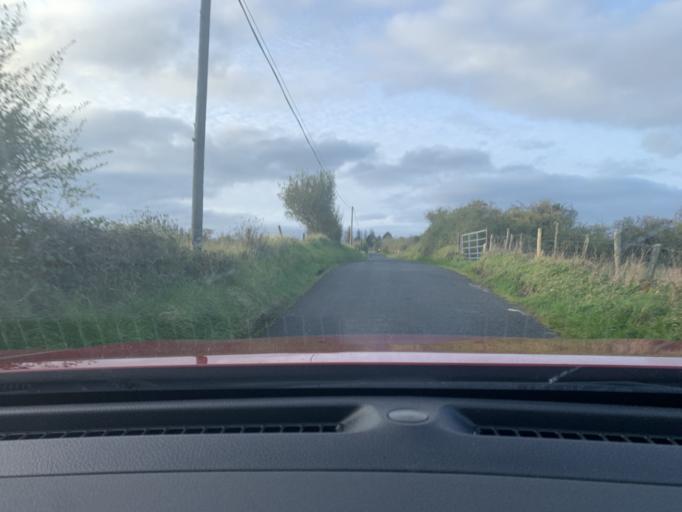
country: IE
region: Connaught
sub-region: Roscommon
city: Ballaghaderreen
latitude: 53.9089
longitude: -8.5807
